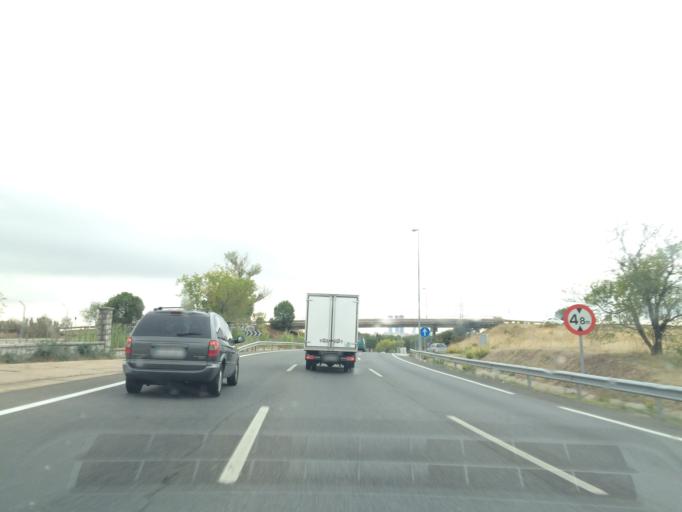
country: ES
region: Madrid
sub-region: Provincia de Madrid
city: Las Tablas
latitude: 40.5377
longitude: -3.6972
